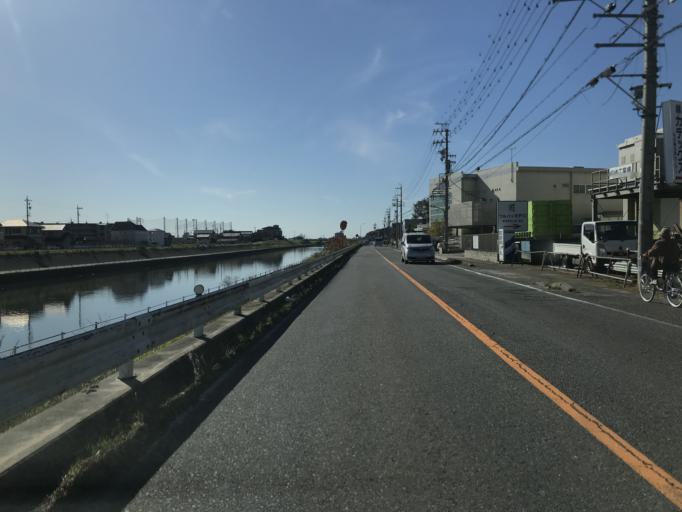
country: JP
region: Aichi
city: Nagoya-shi
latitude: 35.1889
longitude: 136.8473
